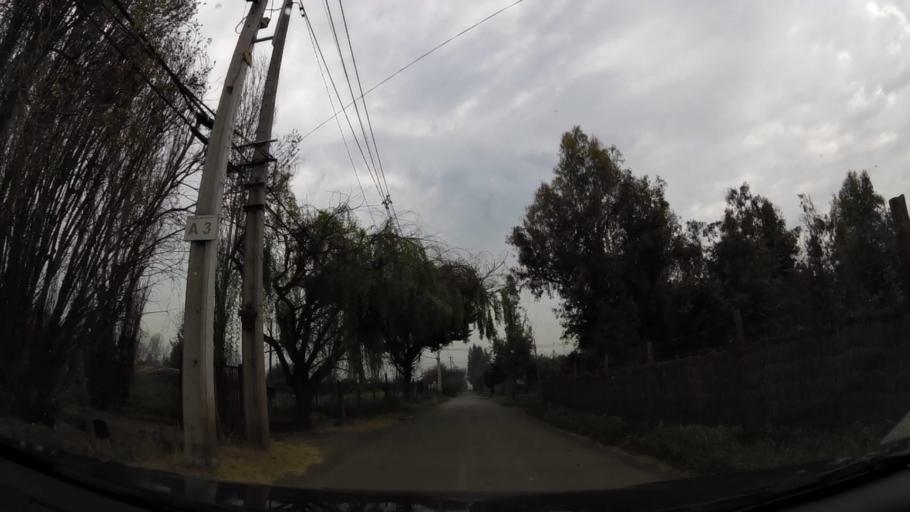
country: CL
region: Santiago Metropolitan
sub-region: Provincia de Chacabuco
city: Lampa
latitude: -33.2432
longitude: -70.7754
